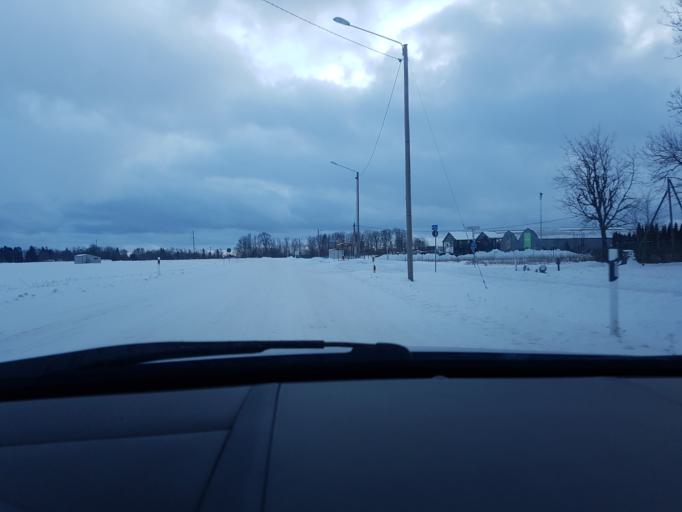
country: EE
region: Harju
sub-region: Kiili vald
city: Kiili
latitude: 59.3433
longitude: 24.8081
